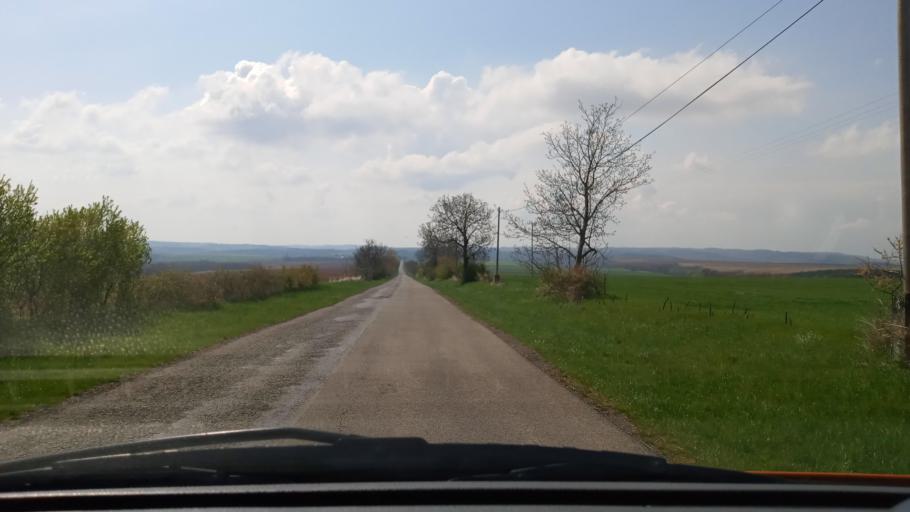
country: HU
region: Baranya
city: Pecsvarad
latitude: 46.1008
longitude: 18.4974
